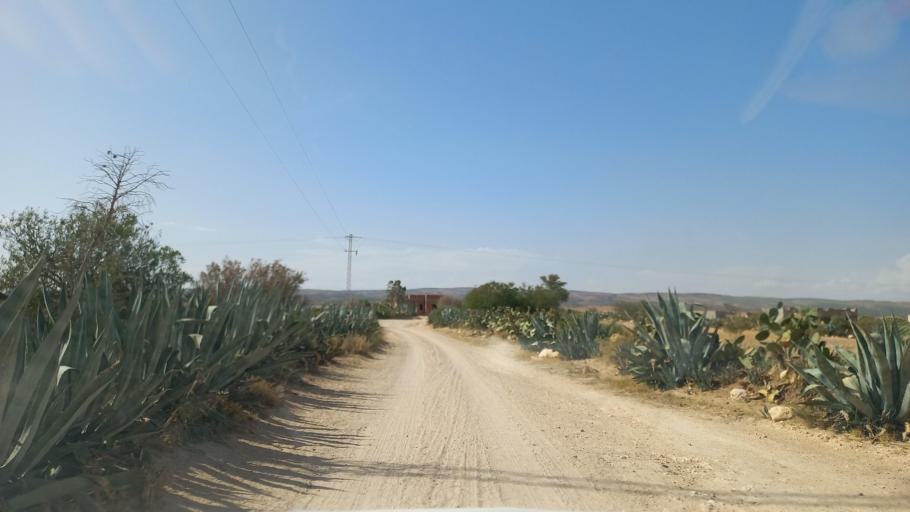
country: TN
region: Al Qasrayn
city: Kasserine
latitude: 35.2746
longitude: 8.9456
